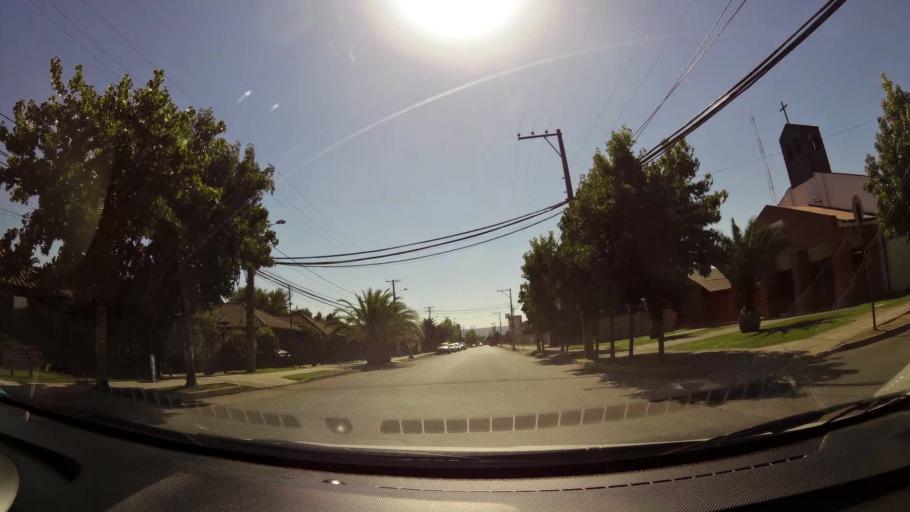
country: CL
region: Maule
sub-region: Provincia de Talca
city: Talca
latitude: -35.4303
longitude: -71.6175
